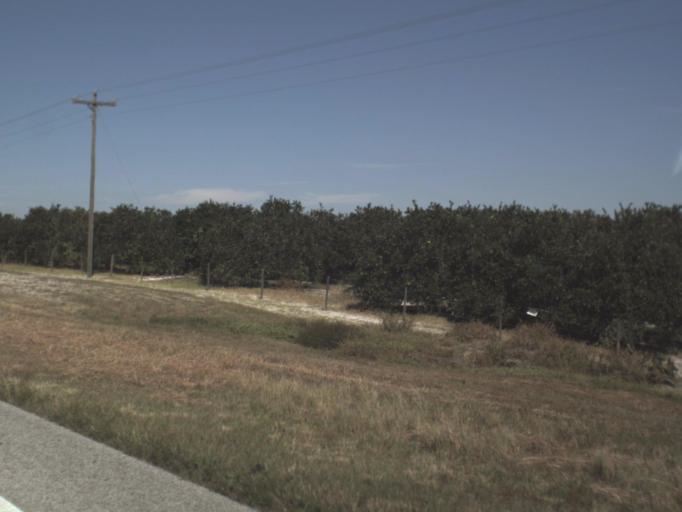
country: US
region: Florida
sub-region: Highlands County
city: Placid Lakes
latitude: 27.1406
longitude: -81.3286
